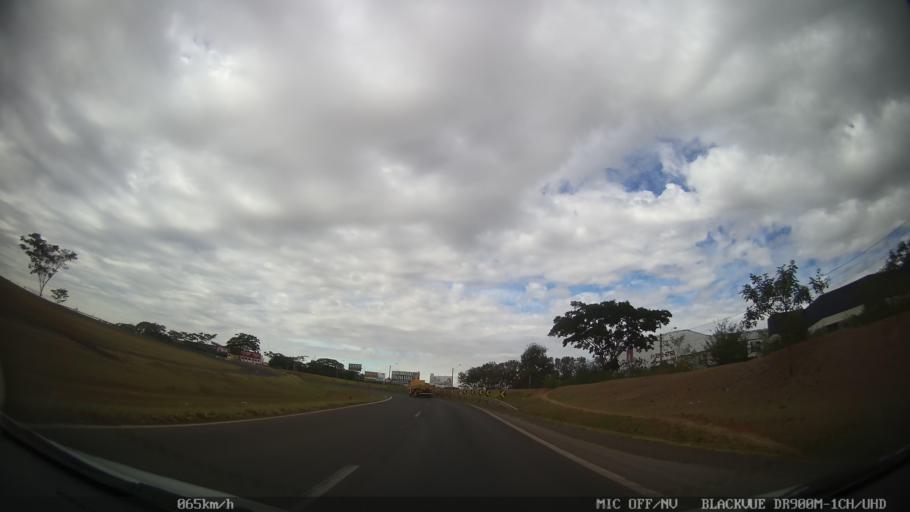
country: BR
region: Sao Paulo
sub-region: Bady Bassitt
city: Bady Bassitt
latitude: -20.8057
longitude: -49.5247
